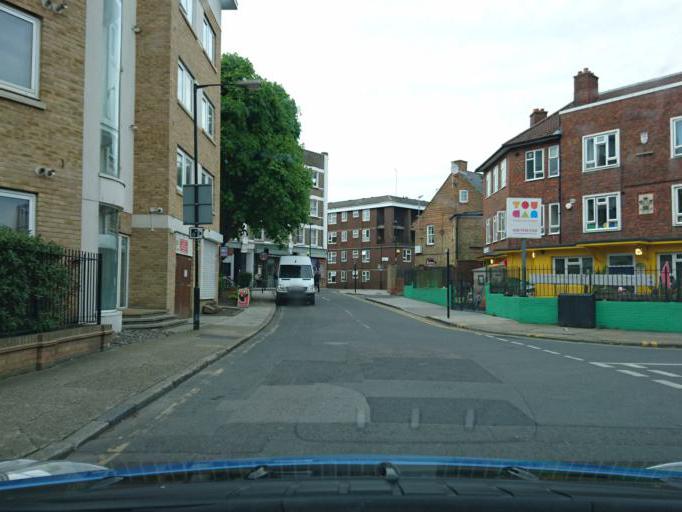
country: GB
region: England
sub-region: Greater London
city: Bethnal Green
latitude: 51.5328
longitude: -0.0649
